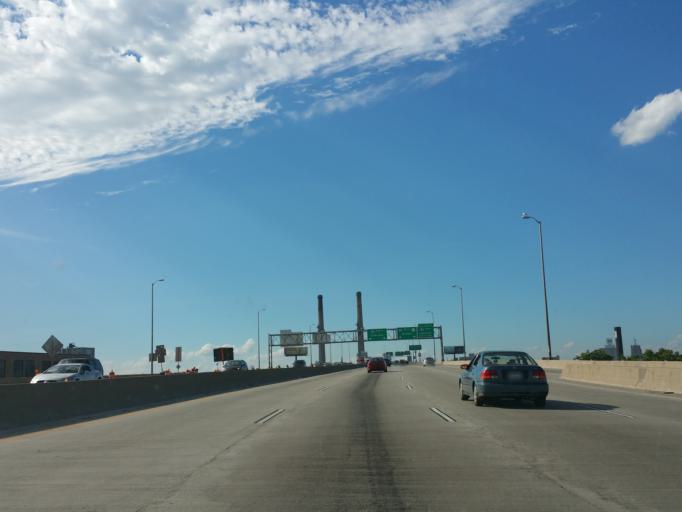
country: US
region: Wisconsin
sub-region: Milwaukee County
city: Milwaukee
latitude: 43.0230
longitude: -87.9208
